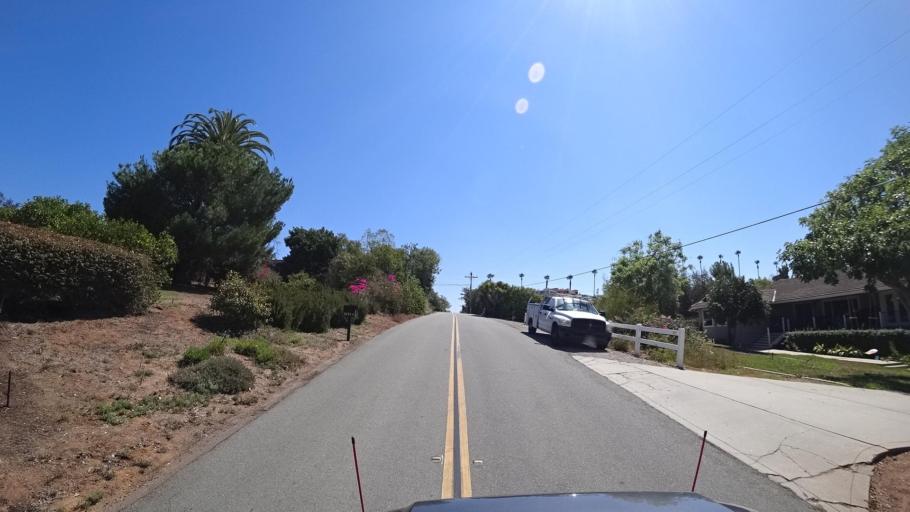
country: US
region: California
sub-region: San Diego County
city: Fallbrook
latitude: 33.3630
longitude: -117.2197
